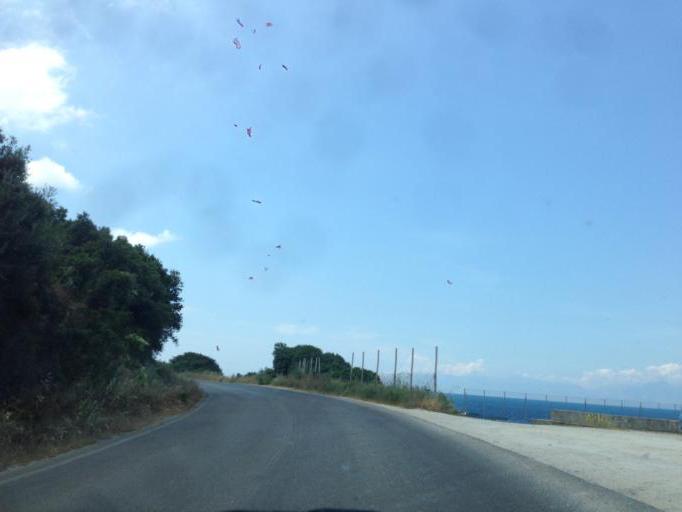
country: GR
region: Ionian Islands
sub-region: Nomos Kerkyras
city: Acharavi
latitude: 39.7911
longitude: 19.9088
